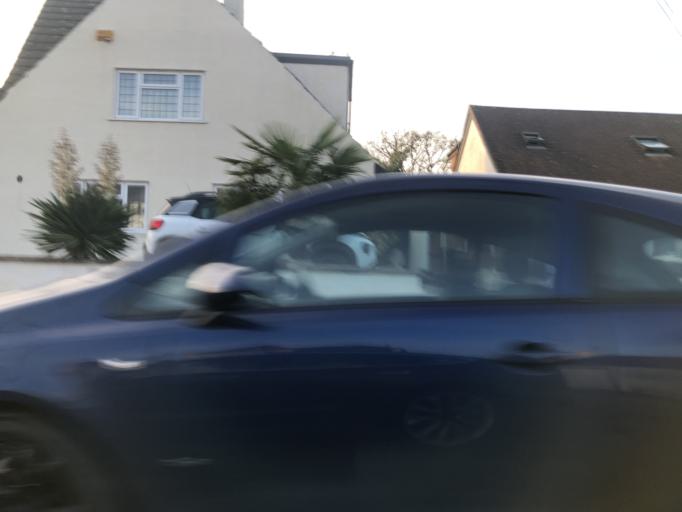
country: GB
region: England
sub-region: Greater London
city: Bexley
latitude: 51.4321
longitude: 0.1660
